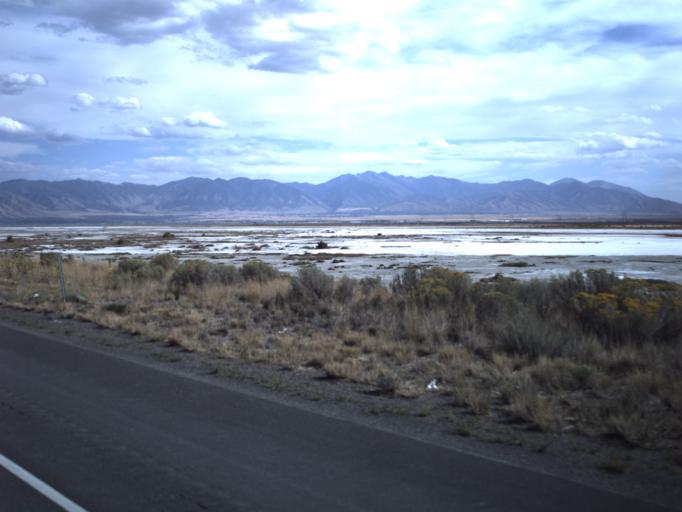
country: US
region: Utah
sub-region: Tooele County
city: Grantsville
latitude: 40.6826
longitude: -112.4340
